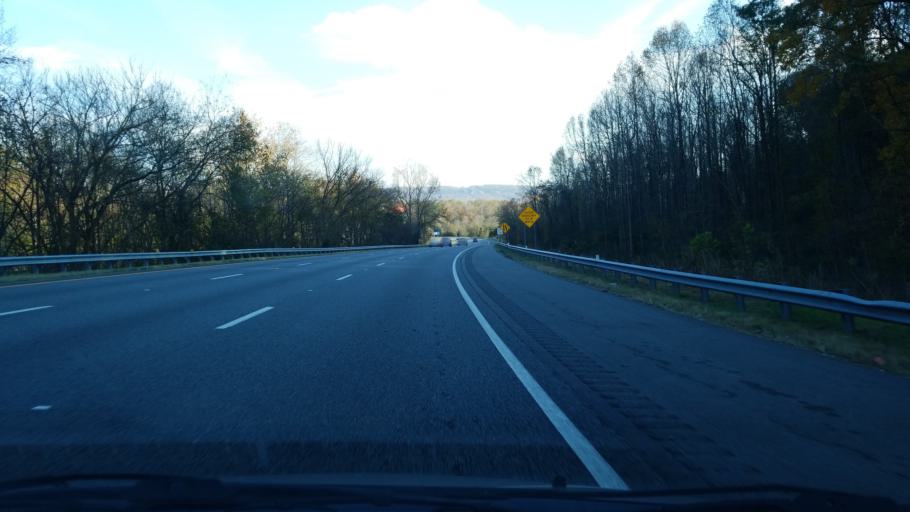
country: US
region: Georgia
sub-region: Walker County
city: Lookout Mountain
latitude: 34.9703
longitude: -85.4410
